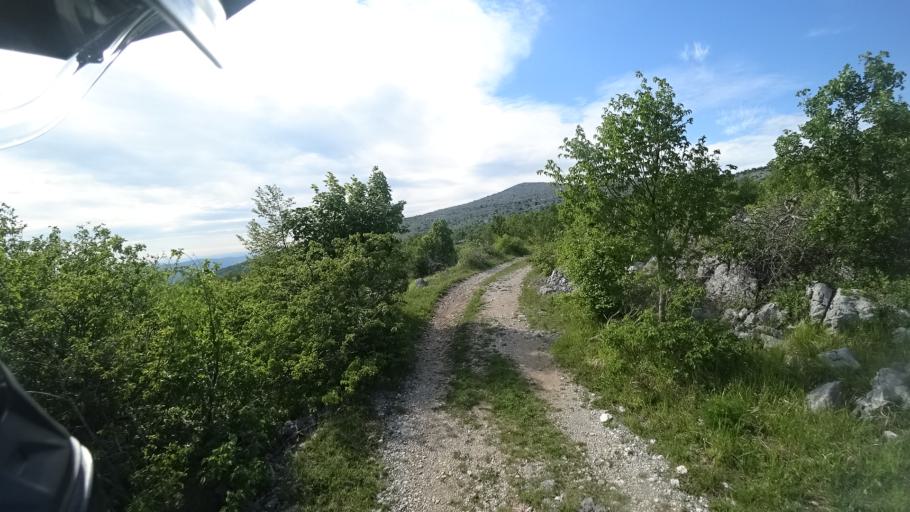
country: HR
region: Splitsko-Dalmatinska
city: Hrvace
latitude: 43.7937
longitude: 16.4344
